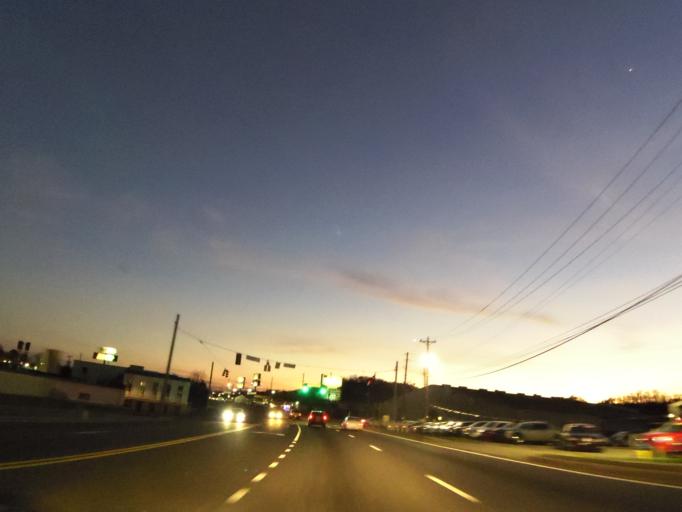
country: US
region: Georgia
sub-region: Whitfield County
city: Dalton
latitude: 34.8010
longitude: -84.9615
